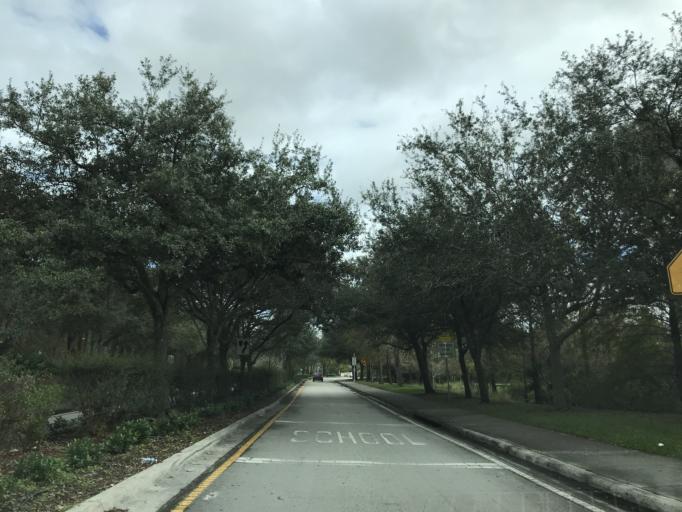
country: US
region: Florida
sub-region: Broward County
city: Coral Springs
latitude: 26.3063
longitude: -80.2769
